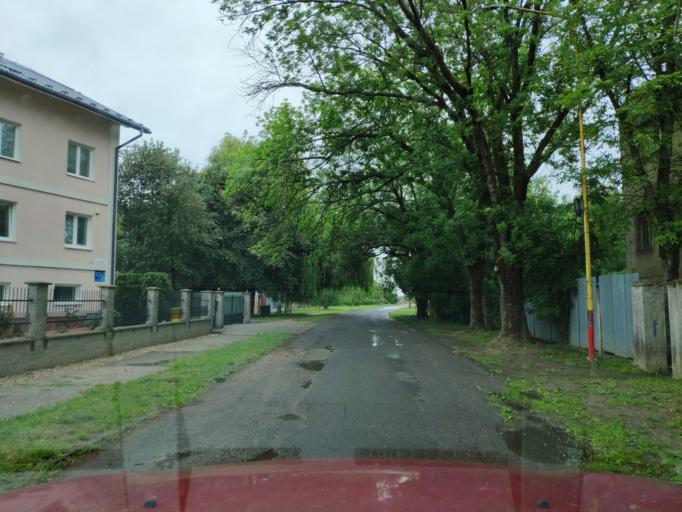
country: SK
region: Kosicky
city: Cierna nad Tisou
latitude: 48.4146
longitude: 22.0862
